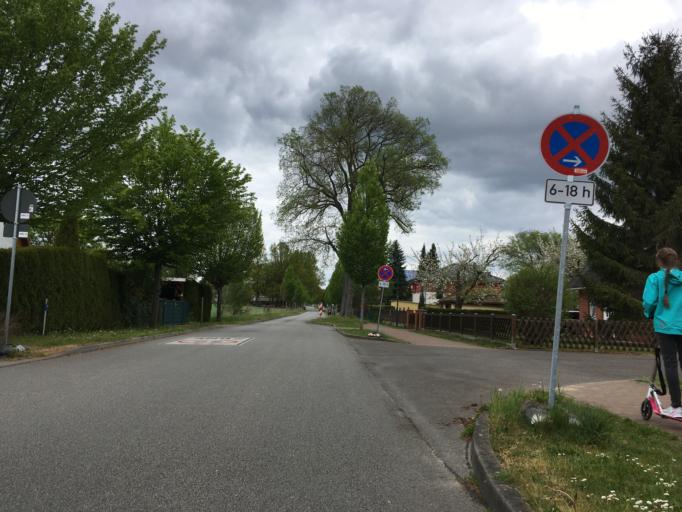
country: DE
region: Berlin
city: Buch
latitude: 52.6575
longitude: 13.5192
